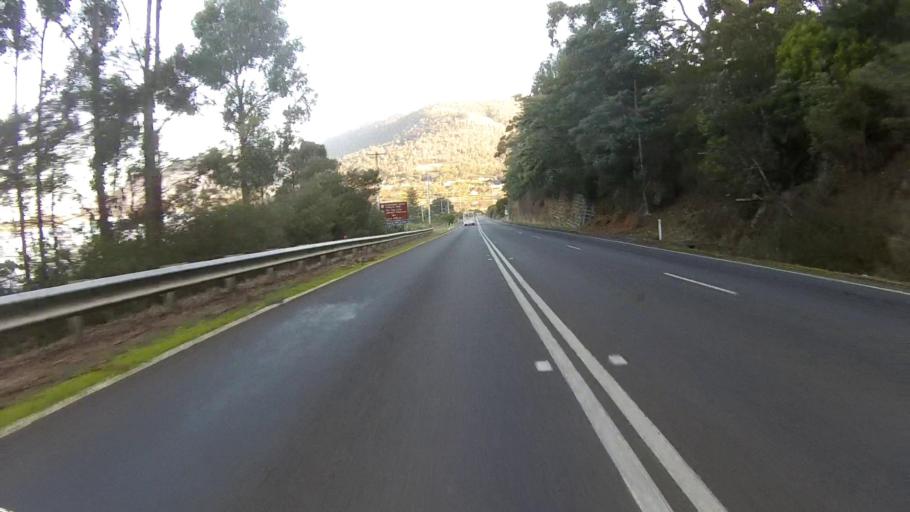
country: AU
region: Tasmania
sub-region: Sorell
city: Sorell
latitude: -43.0110
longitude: 147.9261
